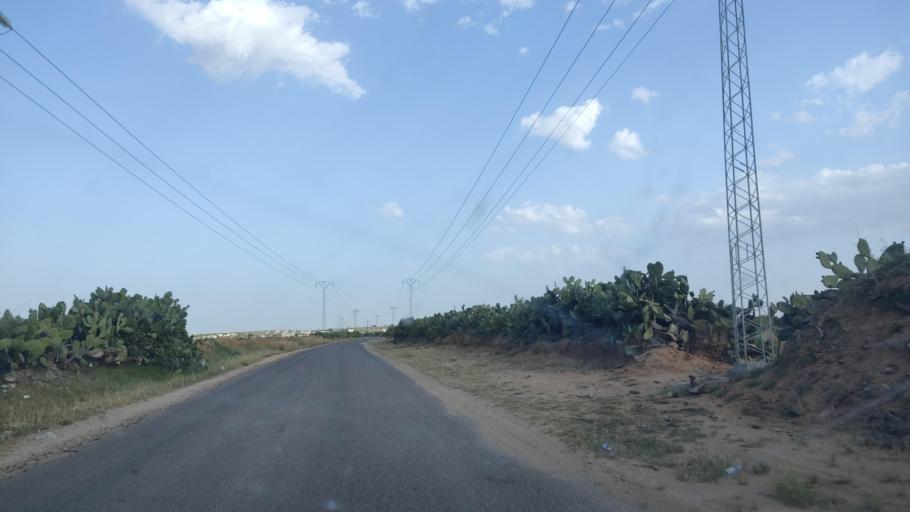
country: TN
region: Safaqis
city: Sfax
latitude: 34.8538
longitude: 10.6083
